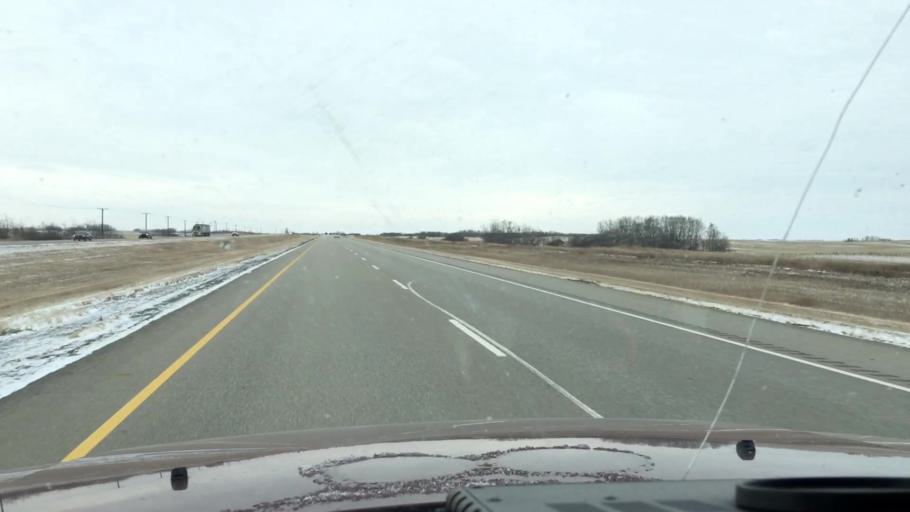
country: CA
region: Saskatchewan
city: Watrous
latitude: 51.3974
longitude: -106.1739
